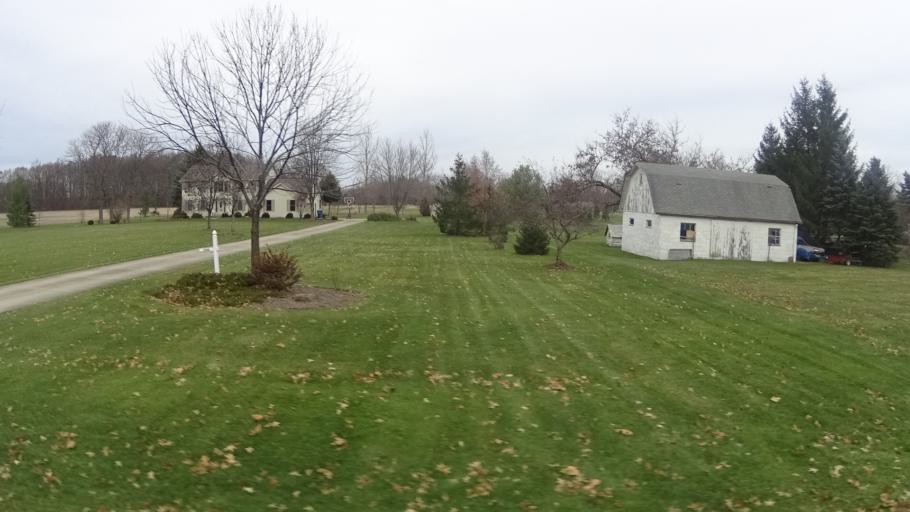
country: US
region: Ohio
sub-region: Cuyahoga County
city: Strongsville
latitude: 41.3049
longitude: -81.8987
